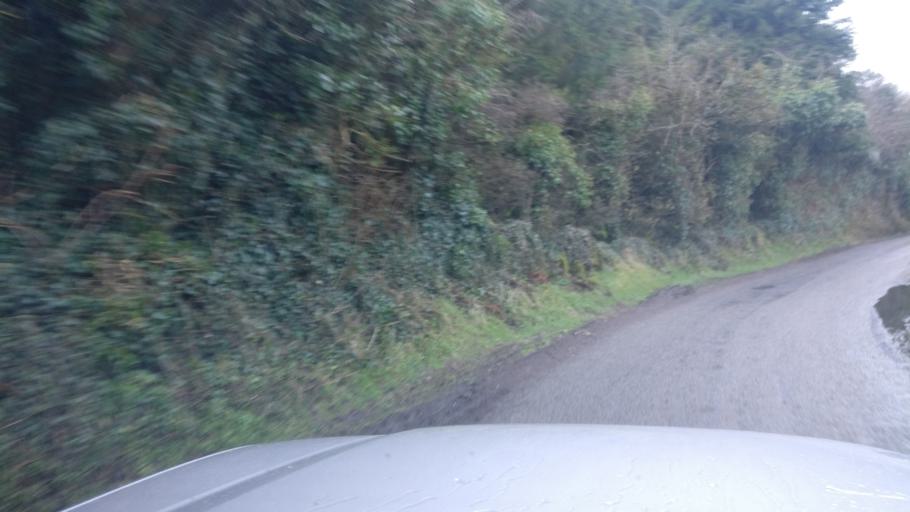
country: IE
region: Connaught
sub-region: County Galway
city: Athenry
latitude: 53.1860
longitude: -8.6959
